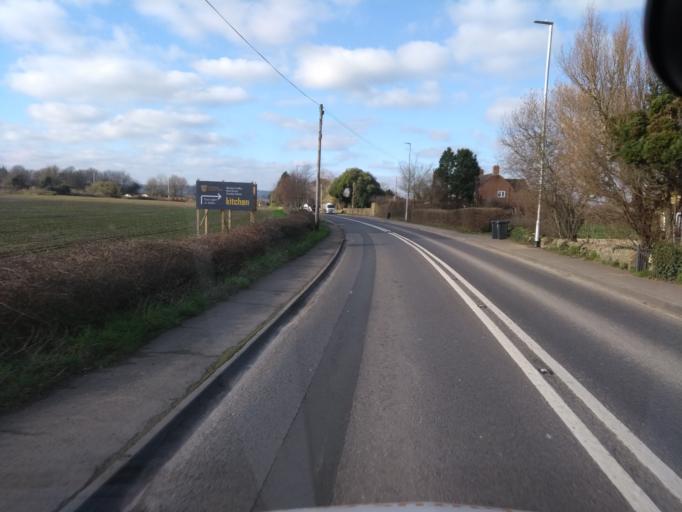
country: GB
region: England
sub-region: Somerset
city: Ilminster
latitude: 50.9335
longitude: -2.9425
